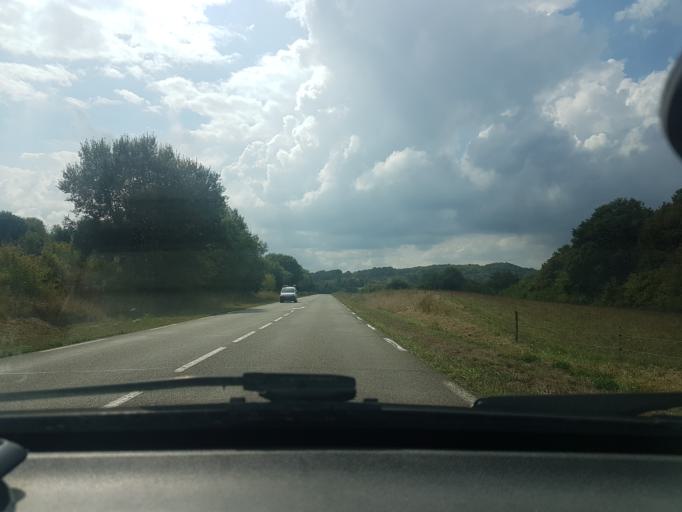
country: FR
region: Franche-Comte
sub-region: Departement de la Haute-Saone
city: Villersexel
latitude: 47.5396
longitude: 6.5442
